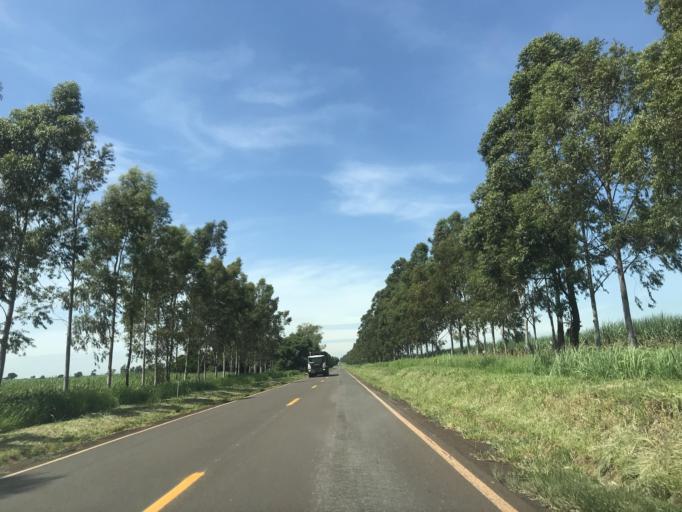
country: BR
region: Parana
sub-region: Paranavai
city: Nova Aurora
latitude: -22.8369
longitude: -52.6565
